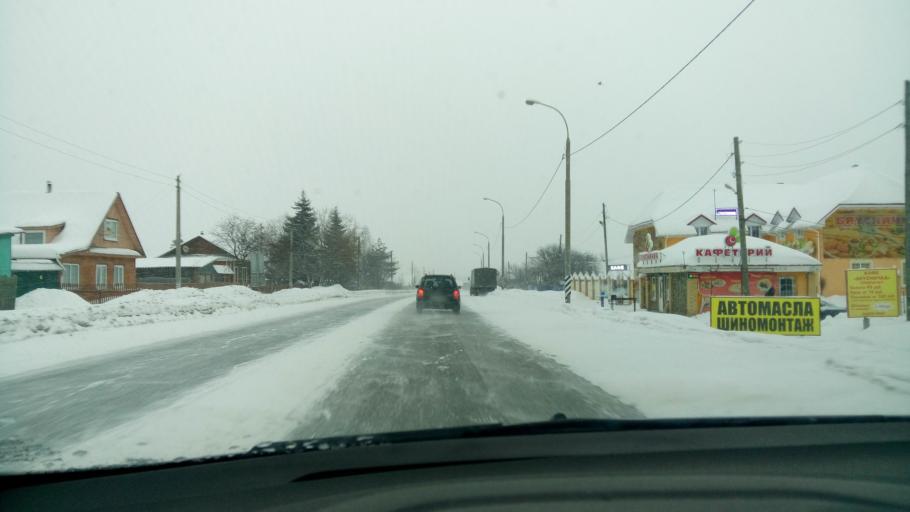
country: RU
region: Sverdlovsk
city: Verkhneye Dubrovo
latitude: 56.7365
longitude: 61.1132
